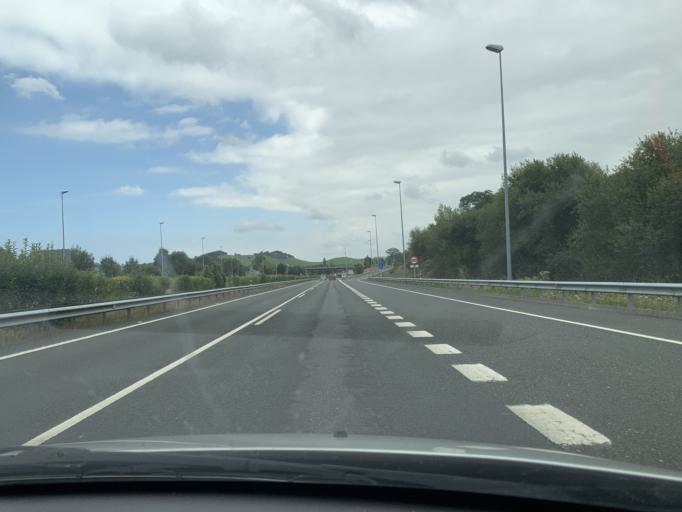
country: ES
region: Cantabria
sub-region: Provincia de Cantabria
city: San Vicente de la Barquera
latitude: 43.3709
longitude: -4.4681
